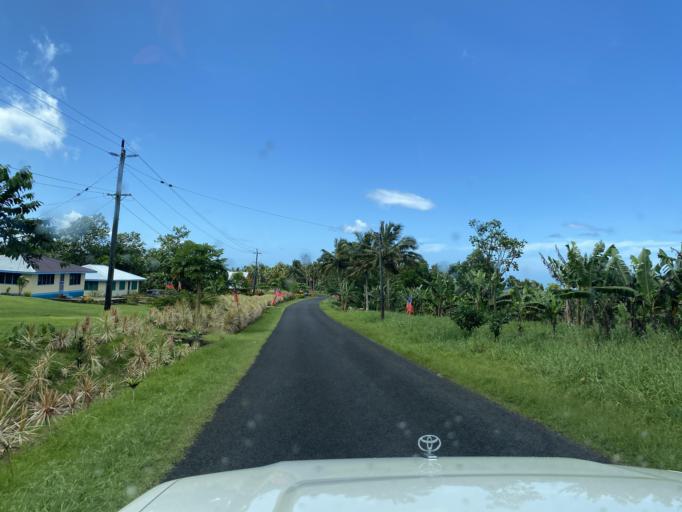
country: WS
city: Matavai
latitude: -13.9940
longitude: -171.5857
